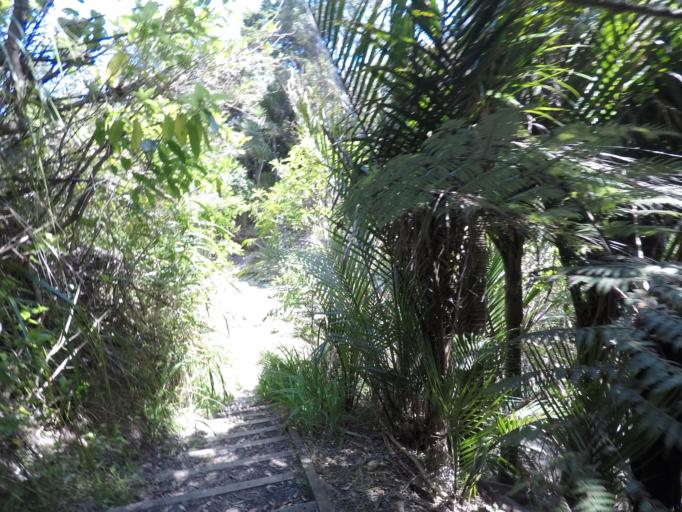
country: NZ
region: Auckland
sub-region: Auckland
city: Titirangi
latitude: -36.9772
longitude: 174.6307
